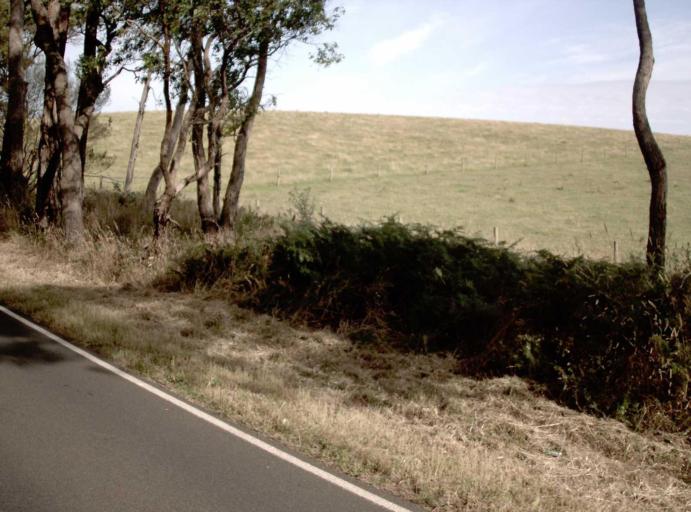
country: AU
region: Victoria
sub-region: Latrobe
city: Morwell
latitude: -38.2785
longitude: 146.3136
